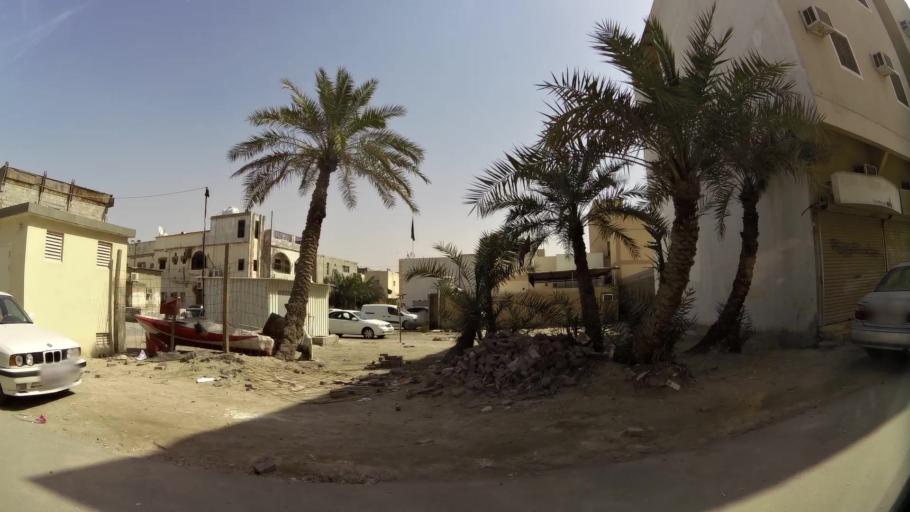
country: BH
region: Manama
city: Jidd Hafs
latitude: 26.1967
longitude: 50.4643
